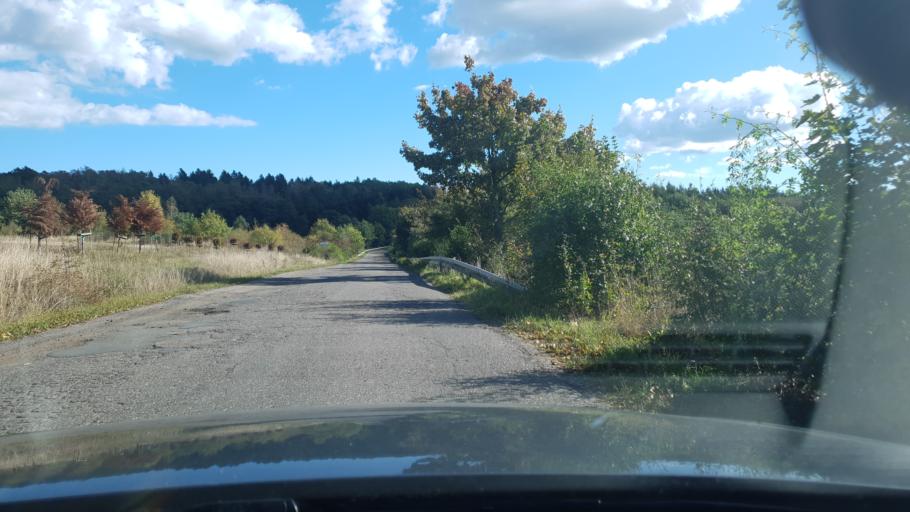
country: PL
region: Pomeranian Voivodeship
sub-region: Powiat pucki
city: Zelistrzewo
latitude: 54.6900
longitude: 18.4215
